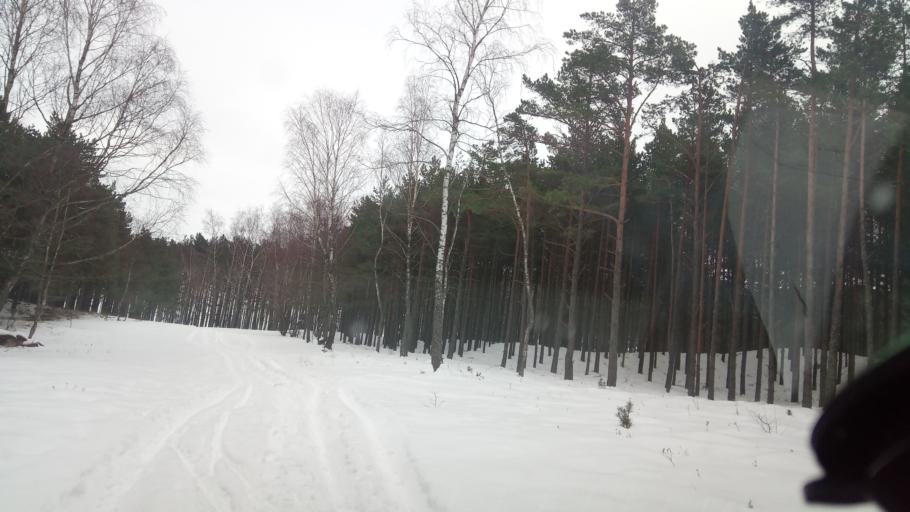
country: LT
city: Neringa
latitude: 55.4203
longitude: 21.1063
